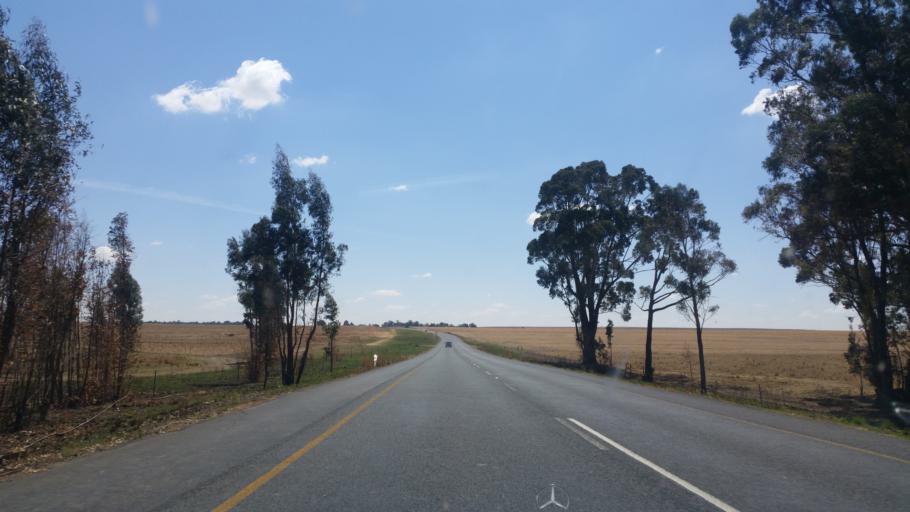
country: ZA
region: Orange Free State
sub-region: Thabo Mofutsanyana District Municipality
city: Reitz
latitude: -28.0922
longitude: 28.6546
